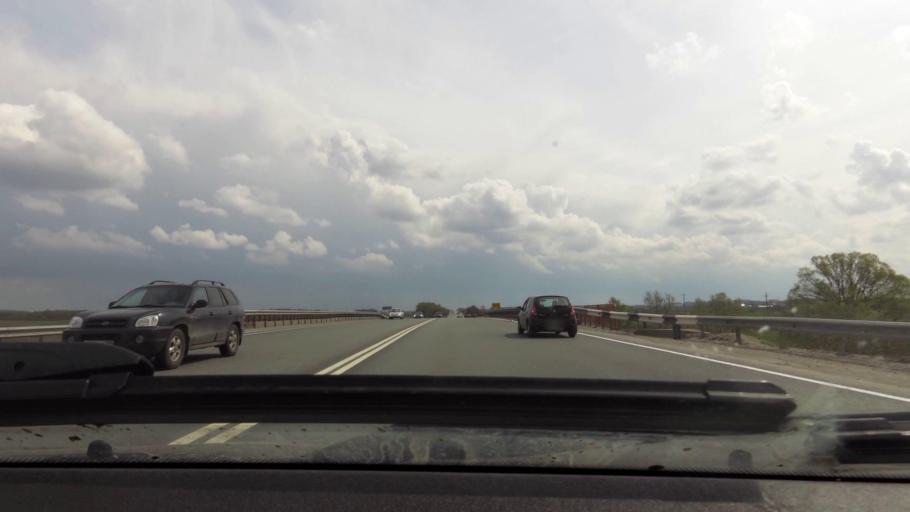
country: RU
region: Rjazan
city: Bagramovo
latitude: 54.7439
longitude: 39.4377
